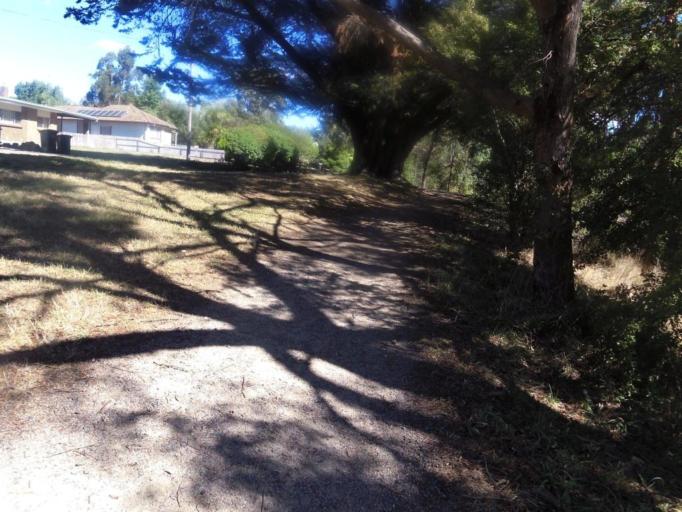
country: AU
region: Victoria
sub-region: Mount Alexander
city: Castlemaine
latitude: -37.2490
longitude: 144.4418
